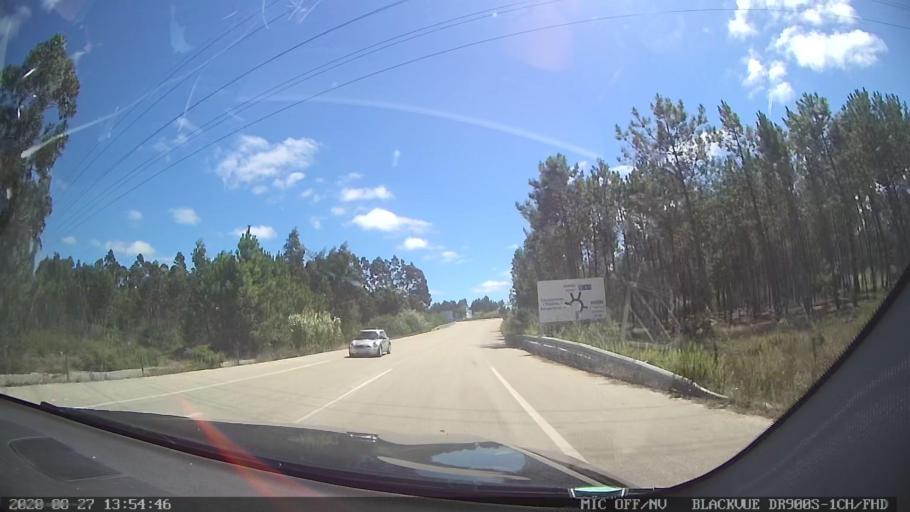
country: PT
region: Coimbra
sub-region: Montemor-O-Velho
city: Arazede
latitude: 40.3330
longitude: -8.7269
